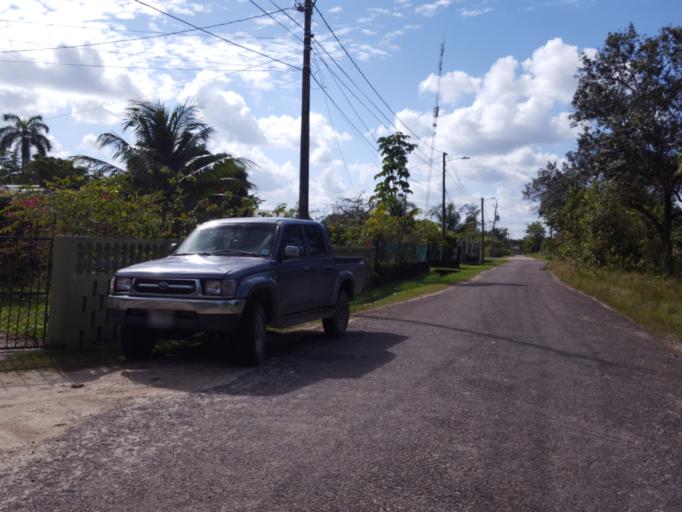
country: BZ
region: Belize
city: Belize City
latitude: 17.5675
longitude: -88.4045
